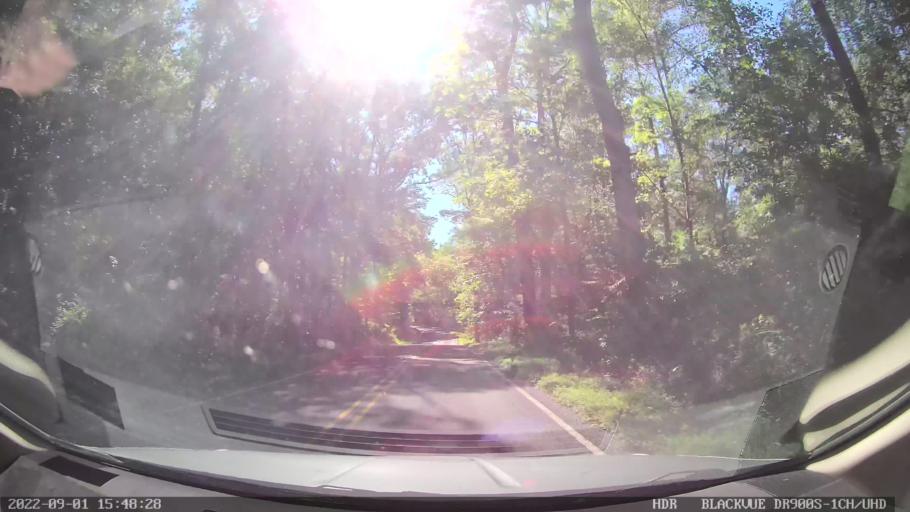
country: US
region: Pennsylvania
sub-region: Berks County
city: Topton
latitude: 40.4713
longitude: -75.7290
